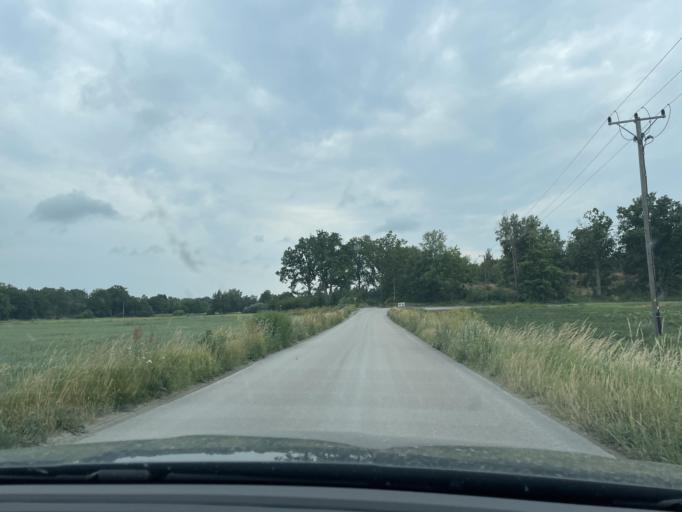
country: SE
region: Blekinge
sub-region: Karlshamns Kommun
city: Morrum
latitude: 56.1658
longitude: 14.7394
